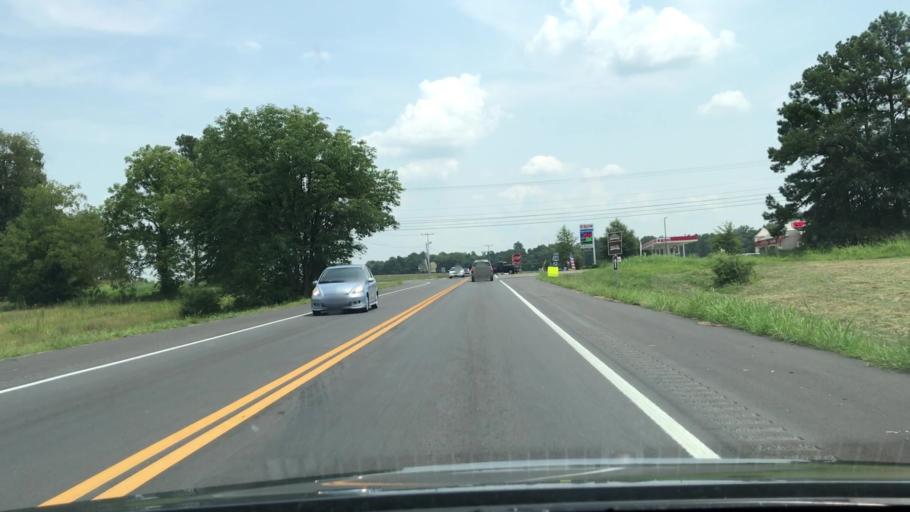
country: US
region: Tennessee
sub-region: Sumner County
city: Portland
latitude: 36.5902
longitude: -86.5940
